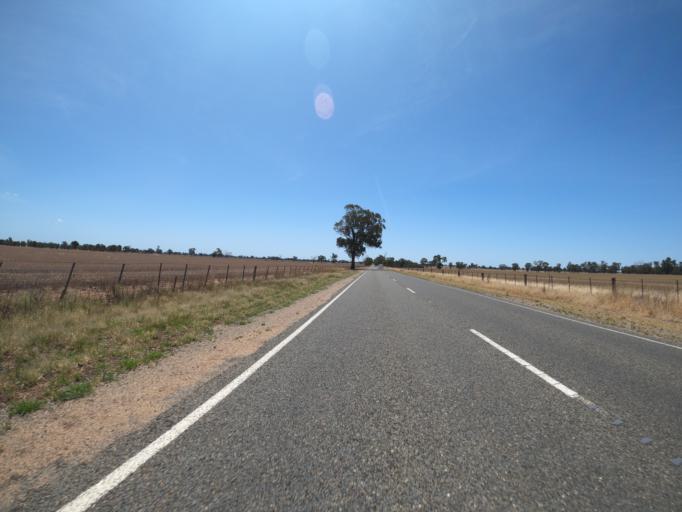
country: AU
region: Victoria
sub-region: Moira
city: Yarrawonga
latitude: -36.0751
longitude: 145.9954
